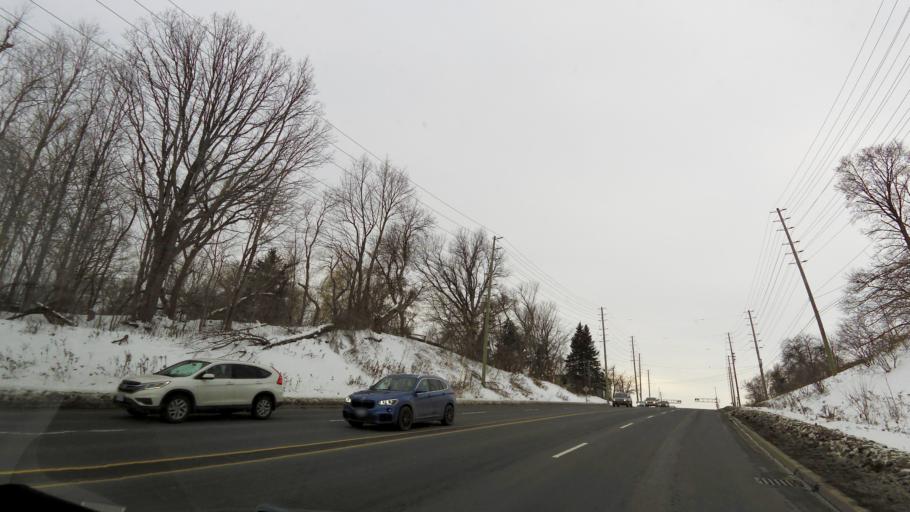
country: CA
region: Ontario
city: Vaughan
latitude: 43.8097
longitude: -79.6317
